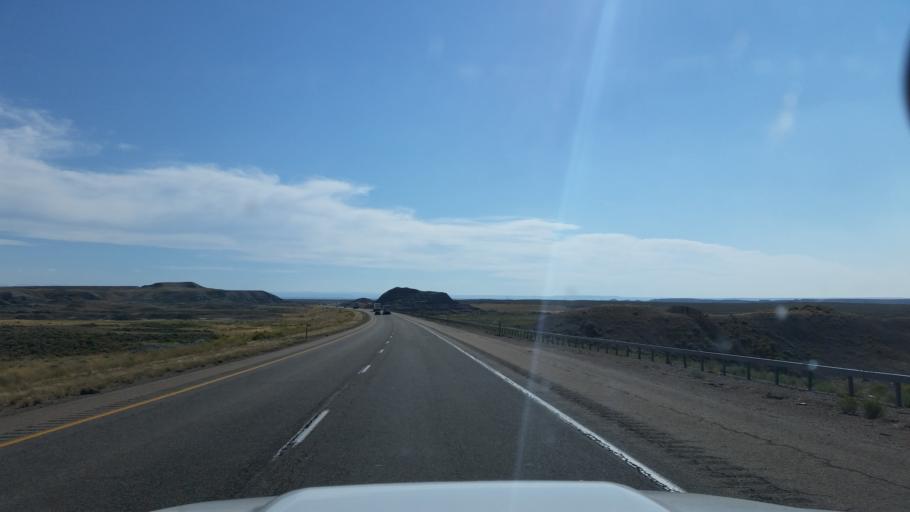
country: US
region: Wyoming
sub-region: Uinta County
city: Lyman
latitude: 41.4239
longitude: -110.1324
